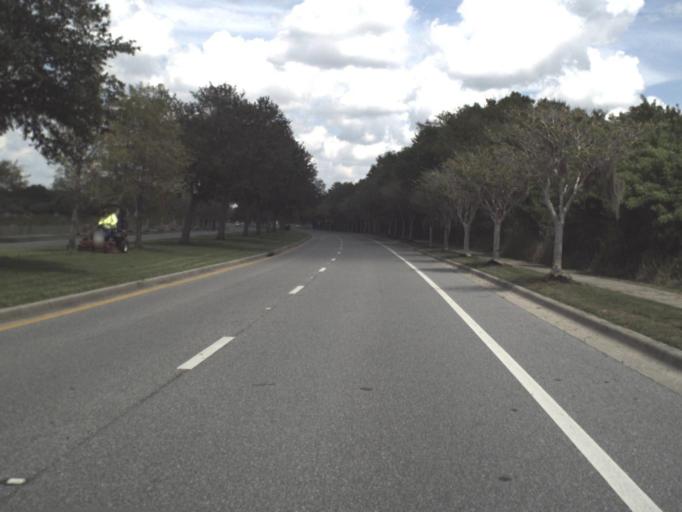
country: US
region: Florida
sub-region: Sarasota County
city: North Sarasota
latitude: 27.3848
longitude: -82.5402
